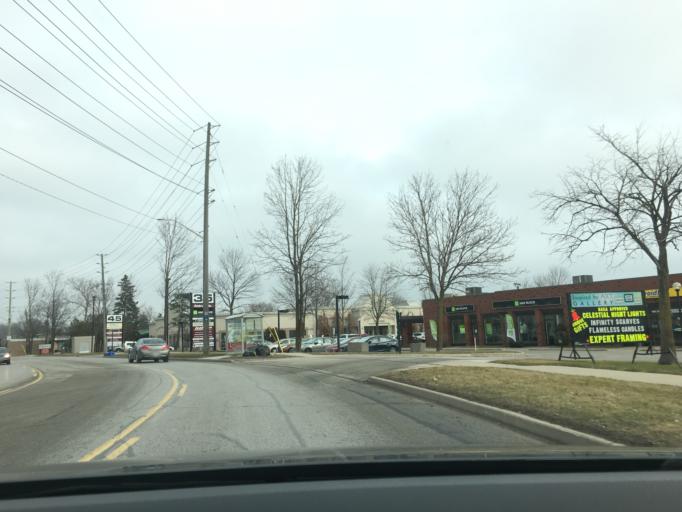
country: CA
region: Ontario
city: Barrie
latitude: 44.3806
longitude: -79.7130
